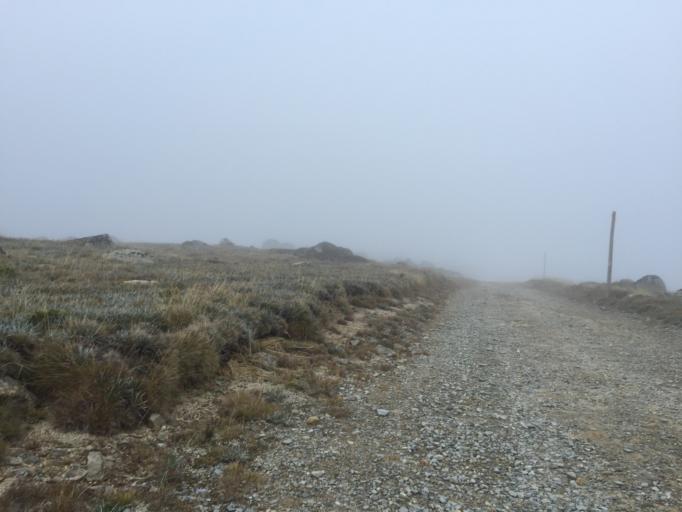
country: AU
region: New South Wales
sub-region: Snowy River
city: Jindabyne
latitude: -36.4517
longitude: 148.2865
